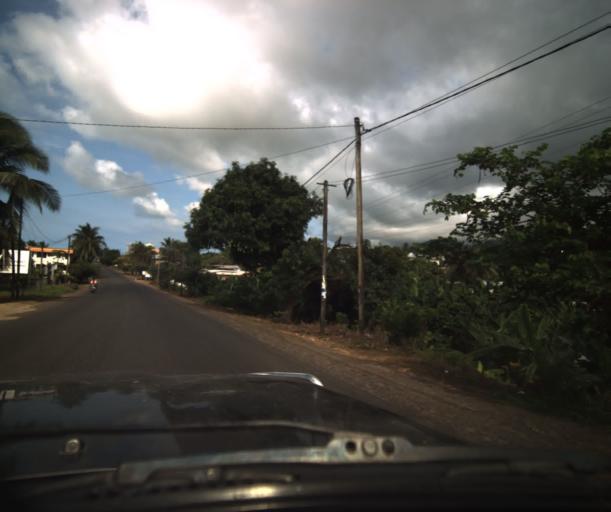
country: CM
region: South-West Province
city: Limbe
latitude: 4.0182
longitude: 9.1716
